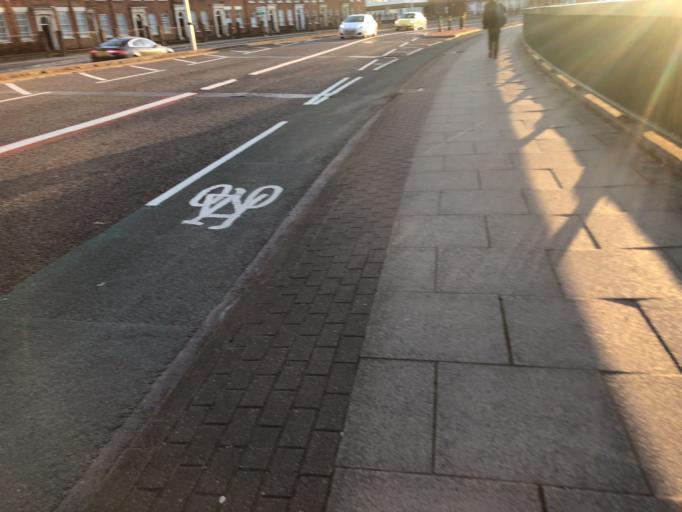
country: GB
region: England
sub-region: City and Borough of Salford
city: Salford
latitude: 53.4834
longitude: -2.2677
